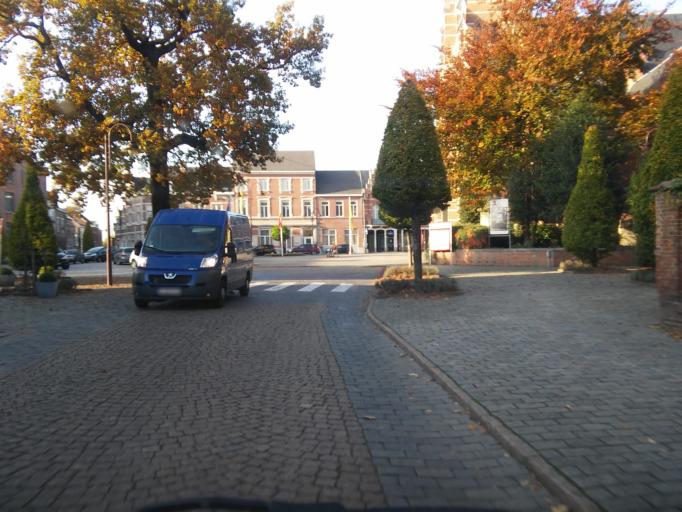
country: BE
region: Flanders
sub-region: Provincie Antwerpen
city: Duffel
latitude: 51.0940
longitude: 4.5007
